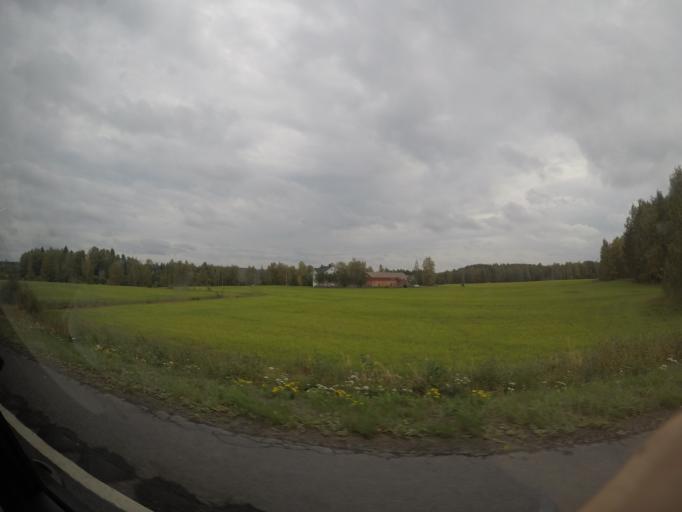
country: FI
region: Haeme
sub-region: Haemeenlinna
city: Parola
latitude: 61.1111
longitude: 24.4140
